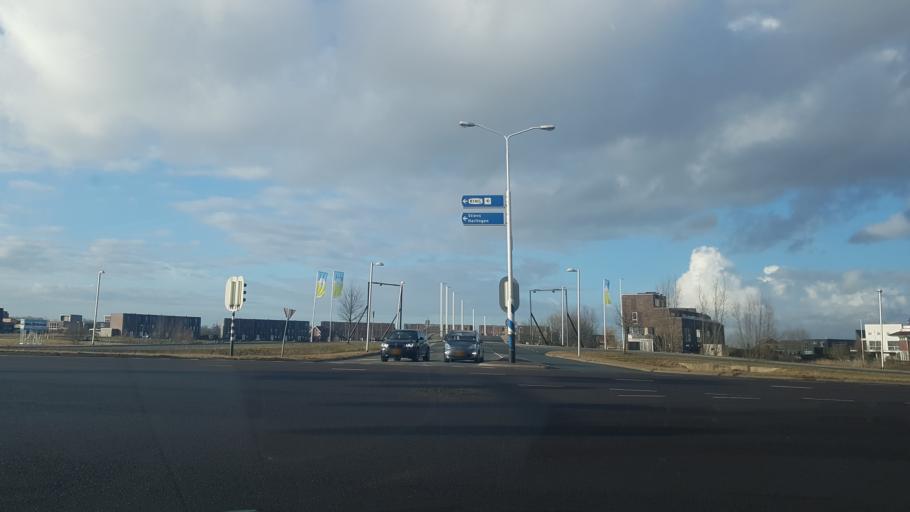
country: NL
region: Friesland
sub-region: Gemeente Leeuwarden
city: Camminghaburen
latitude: 53.2170
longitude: 5.8293
